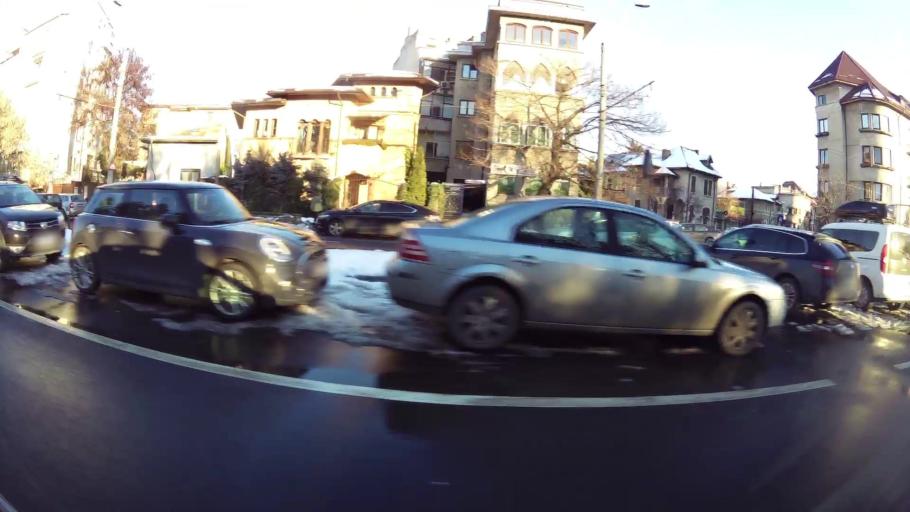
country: RO
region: Bucuresti
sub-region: Municipiul Bucuresti
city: Bucuresti
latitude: 44.4359
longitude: 26.0667
